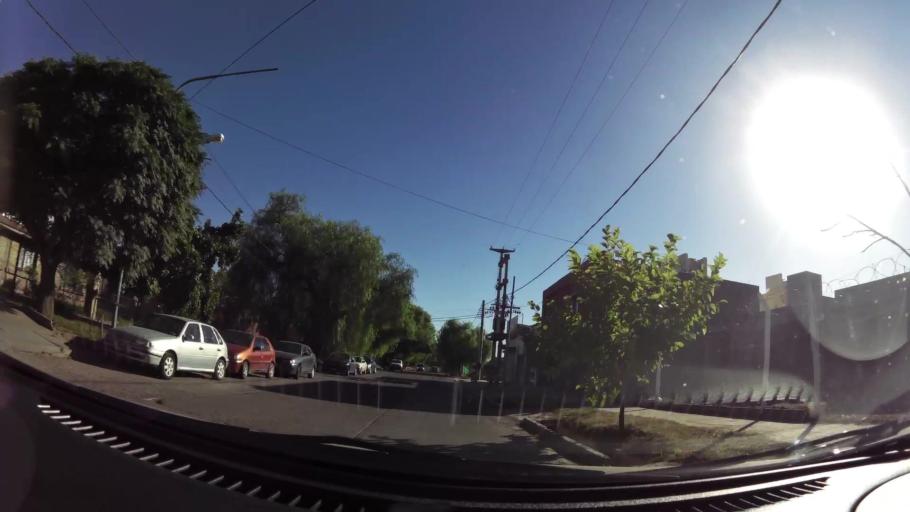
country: AR
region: Mendoza
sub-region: Departamento de Godoy Cruz
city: Godoy Cruz
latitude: -32.9344
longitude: -68.8317
